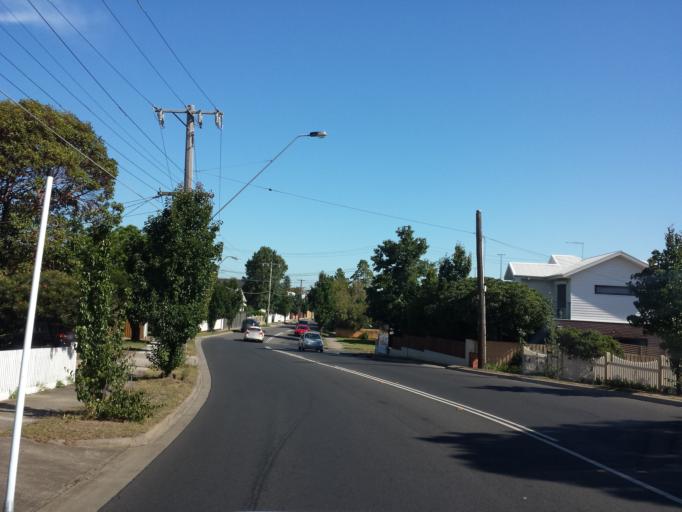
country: AU
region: Victoria
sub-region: Moonee Valley
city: Moonee Ponds
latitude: -37.7632
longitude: 144.9059
